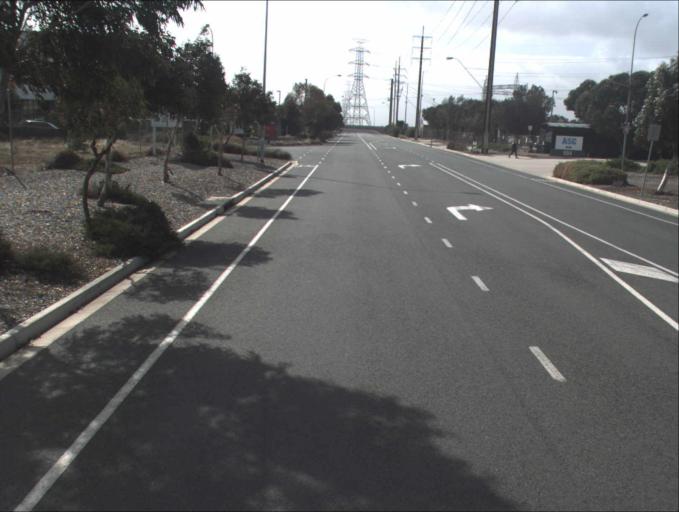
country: AU
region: South Australia
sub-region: Port Adelaide Enfield
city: Birkenhead
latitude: -34.7820
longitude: 138.5079
